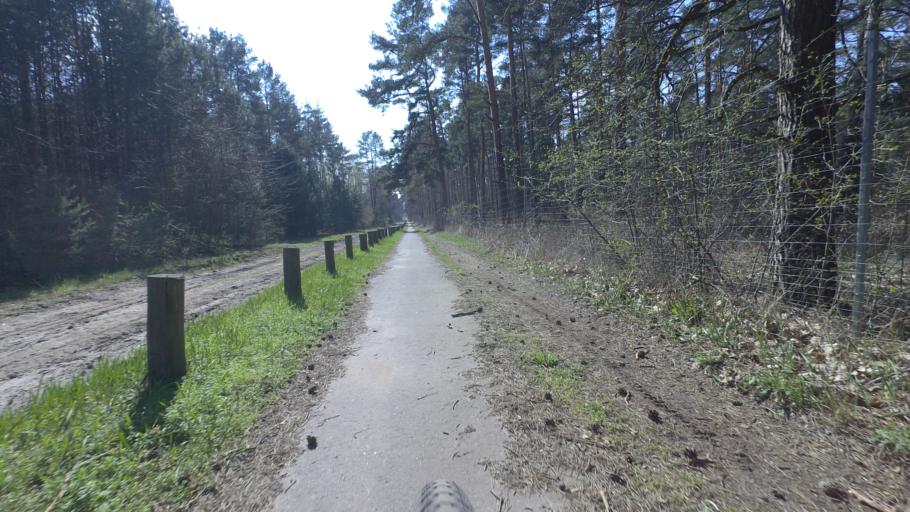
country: DE
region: Brandenburg
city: Mittenwalde
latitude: 52.2017
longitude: 13.5472
